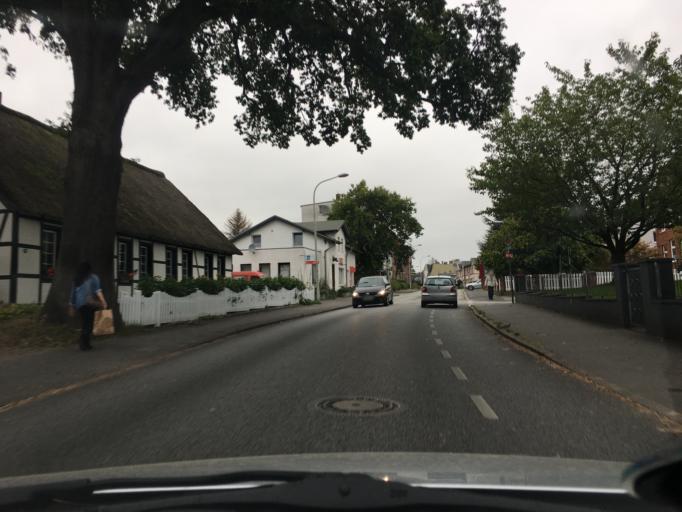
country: DE
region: Schleswig-Holstein
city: Strande
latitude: 54.3986
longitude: 10.1694
